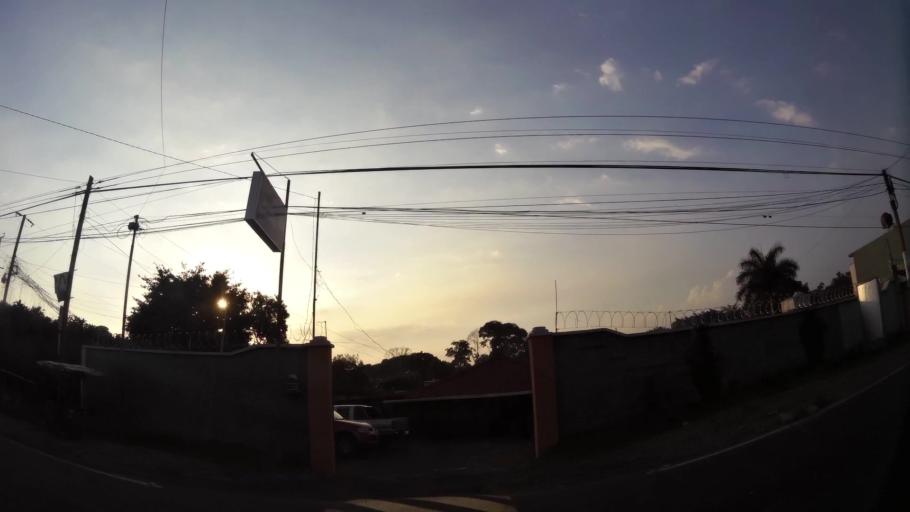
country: GT
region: Retalhuleu
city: San Sebastian
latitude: 14.5630
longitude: -91.6533
